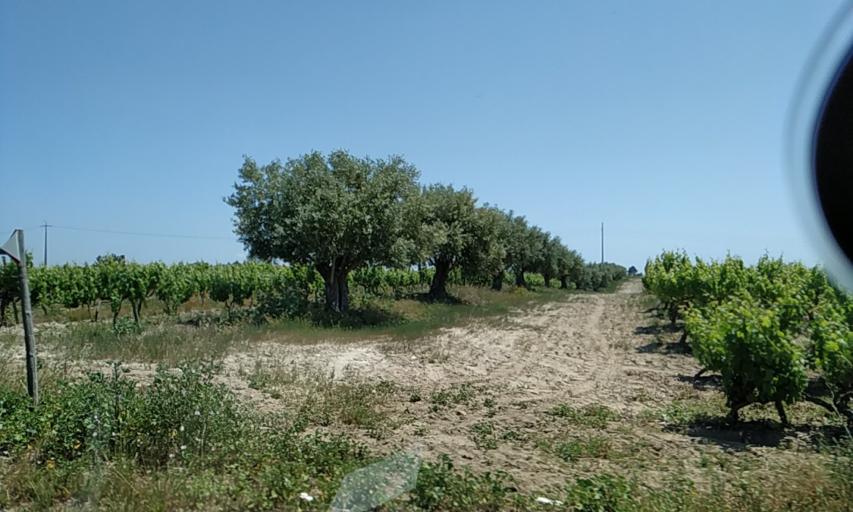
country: PT
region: Setubal
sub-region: Palmela
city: Palmela
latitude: 38.5983
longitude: -8.8325
